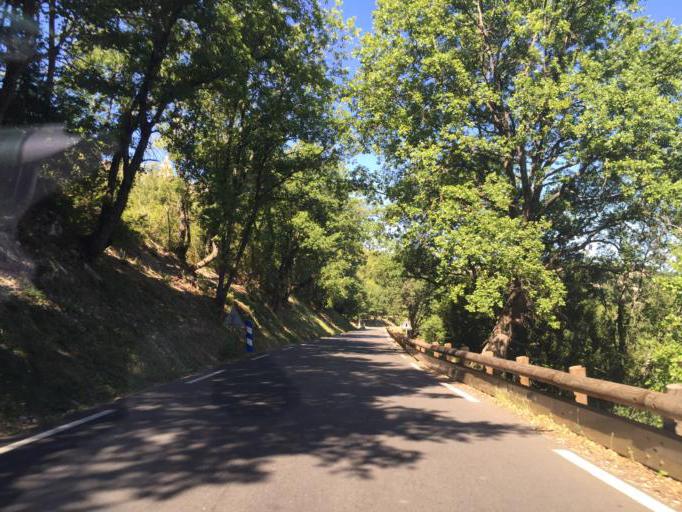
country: FR
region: Provence-Alpes-Cote d'Azur
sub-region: Departement du Vaucluse
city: Venasque
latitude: 43.9969
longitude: 5.1507
